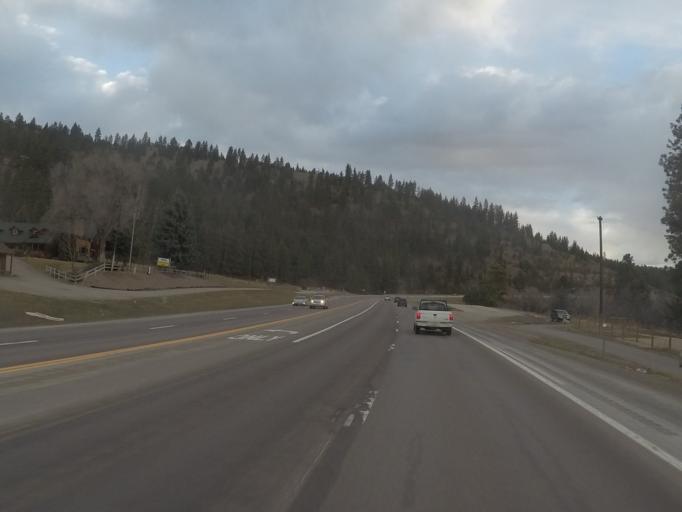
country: US
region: Montana
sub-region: Missoula County
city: Lolo
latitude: 46.8035
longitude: -114.0975
